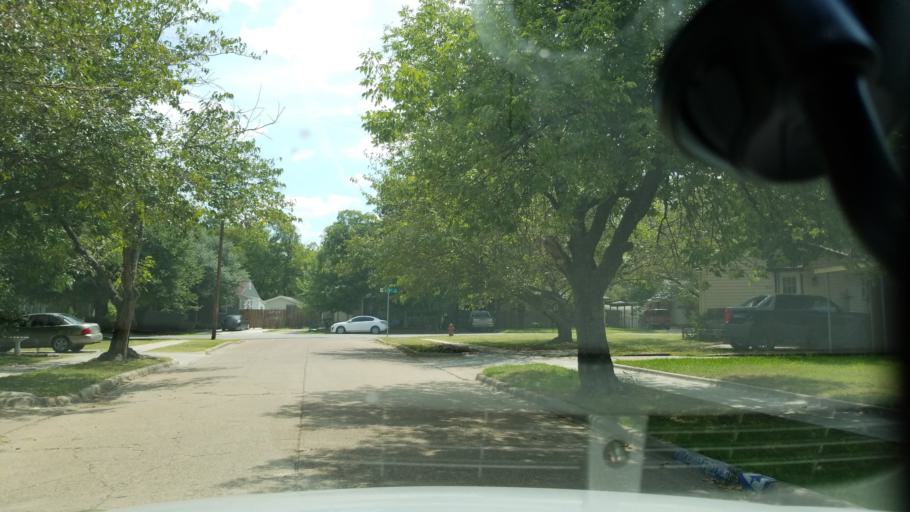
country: US
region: Texas
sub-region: Dallas County
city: Grand Prairie
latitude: 32.7567
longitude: -96.9786
